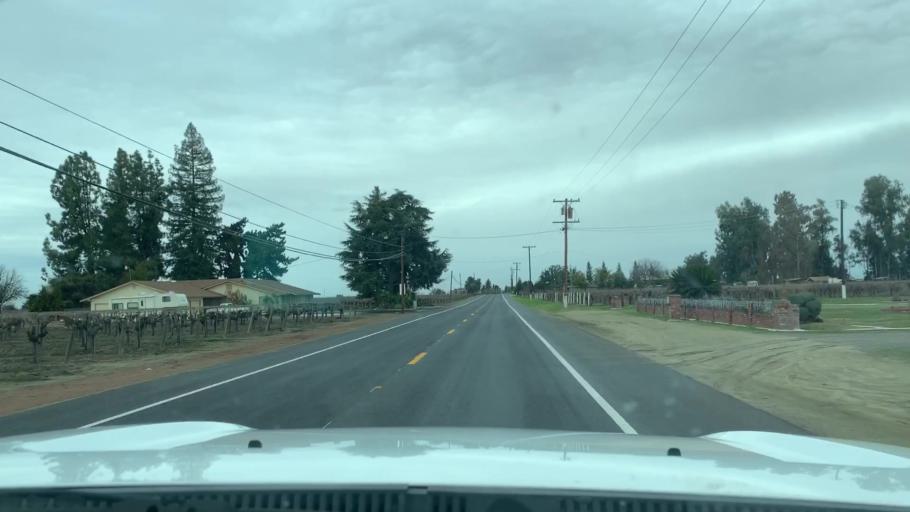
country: US
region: California
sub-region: Fresno County
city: Selma
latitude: 36.5489
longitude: -119.6827
